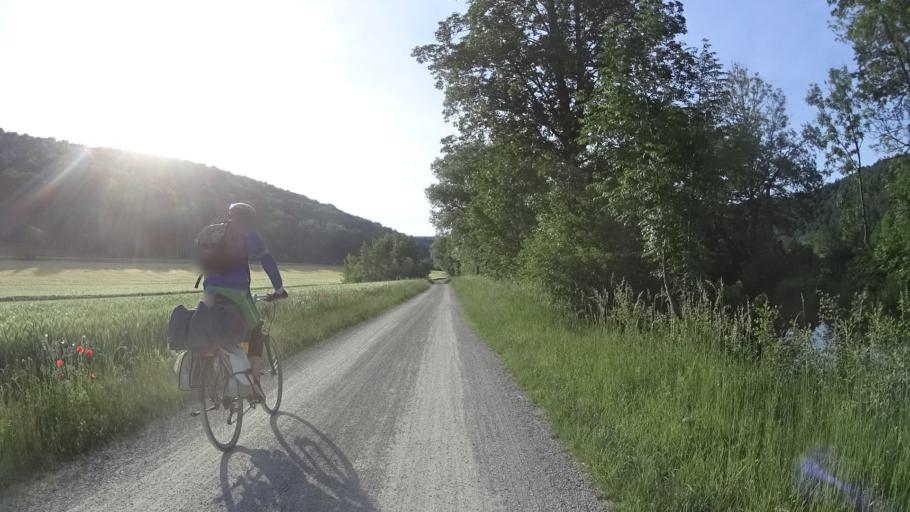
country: DE
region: Bavaria
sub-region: Lower Bavaria
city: Riedenburg
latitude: 48.9805
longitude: 11.6397
